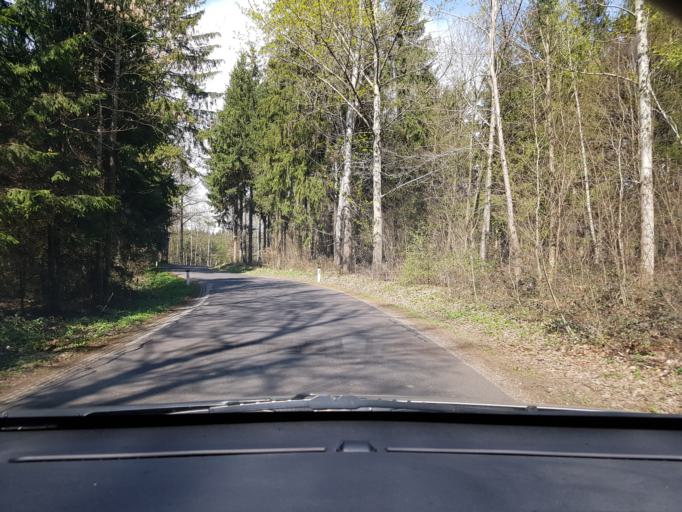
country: AT
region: Upper Austria
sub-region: Politischer Bezirk Linz-Land
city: Ansfelden
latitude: 48.2005
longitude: 14.3294
